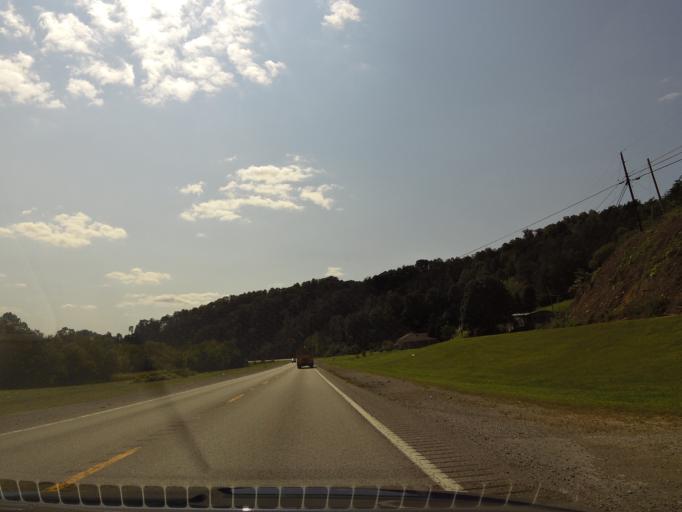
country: US
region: Kentucky
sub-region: Harlan County
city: Loyall
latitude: 36.8223
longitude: -83.4893
